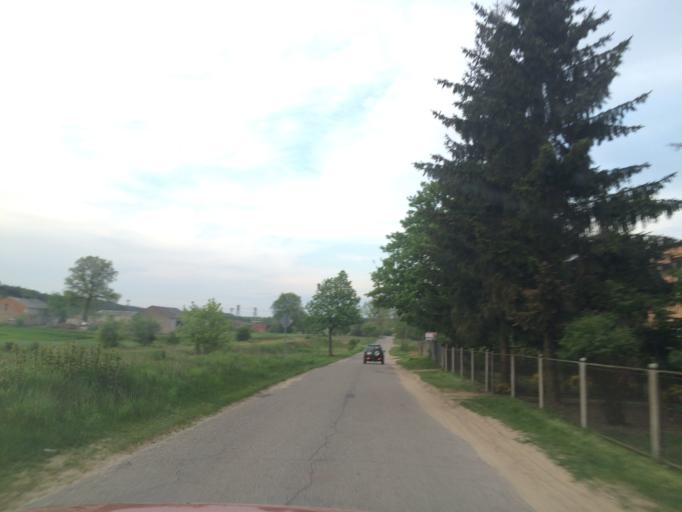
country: PL
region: Warmian-Masurian Voivodeship
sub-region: Powiat nowomiejski
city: Kurzetnik
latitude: 53.3983
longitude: 19.5360
